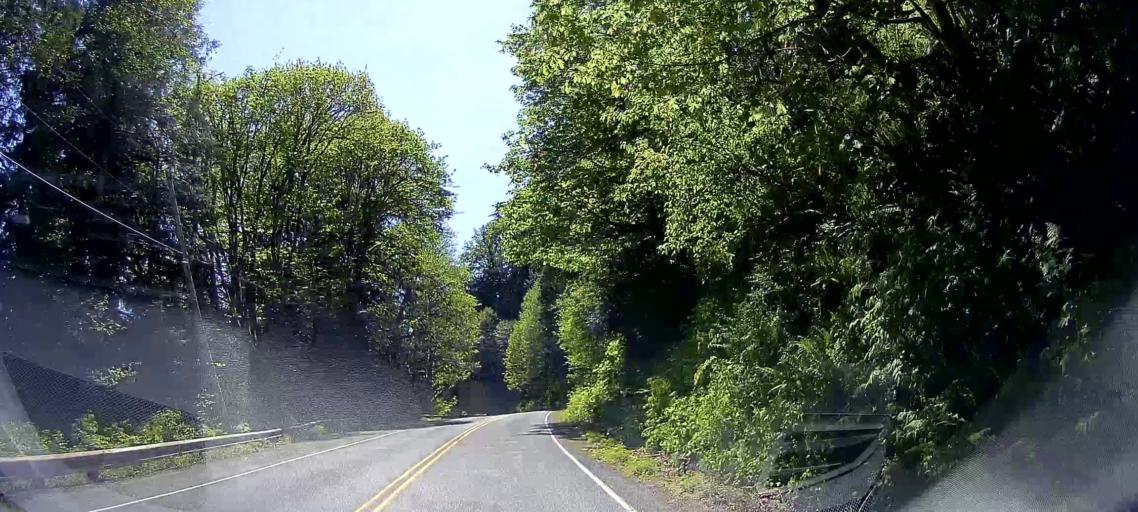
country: US
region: Washington
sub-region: Snohomish County
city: Darrington
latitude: 48.4791
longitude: -121.6495
